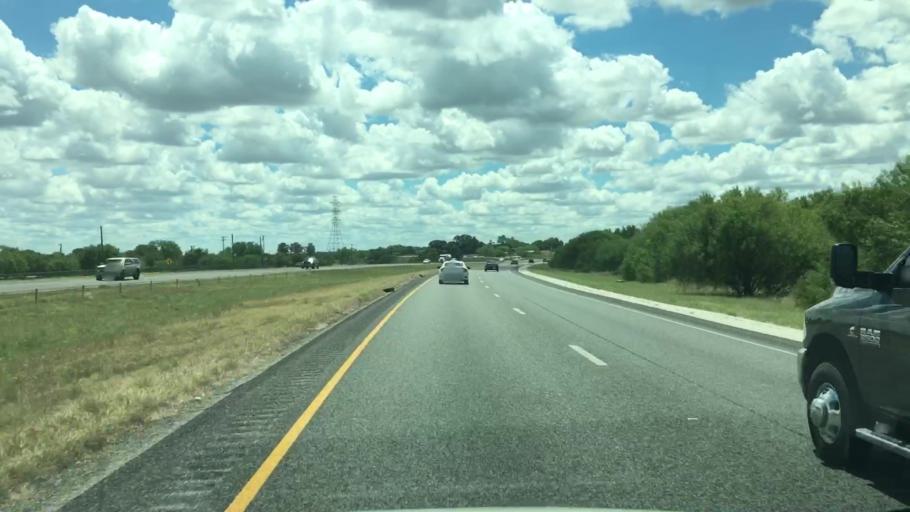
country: US
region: Texas
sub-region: Bexar County
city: Elmendorf
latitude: 29.2525
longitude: -98.3951
